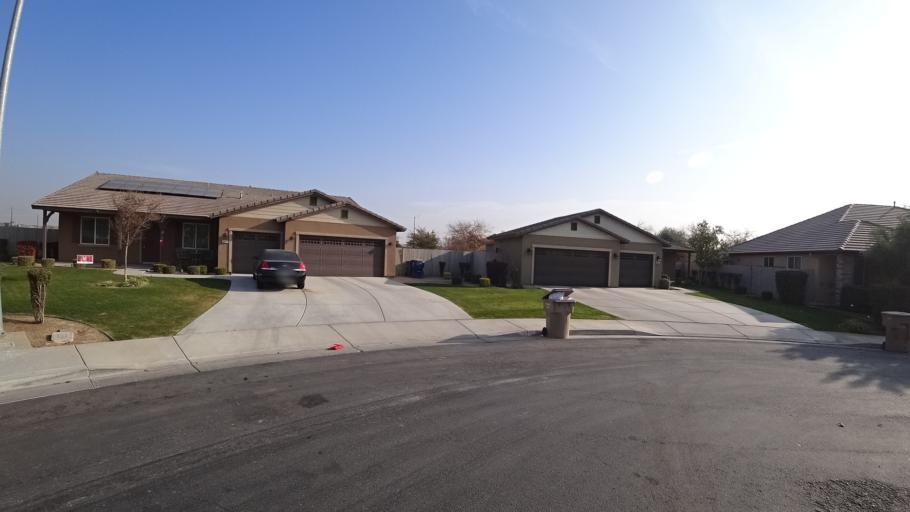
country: US
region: California
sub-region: Kern County
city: Greenacres
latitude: 35.4375
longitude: -119.1197
